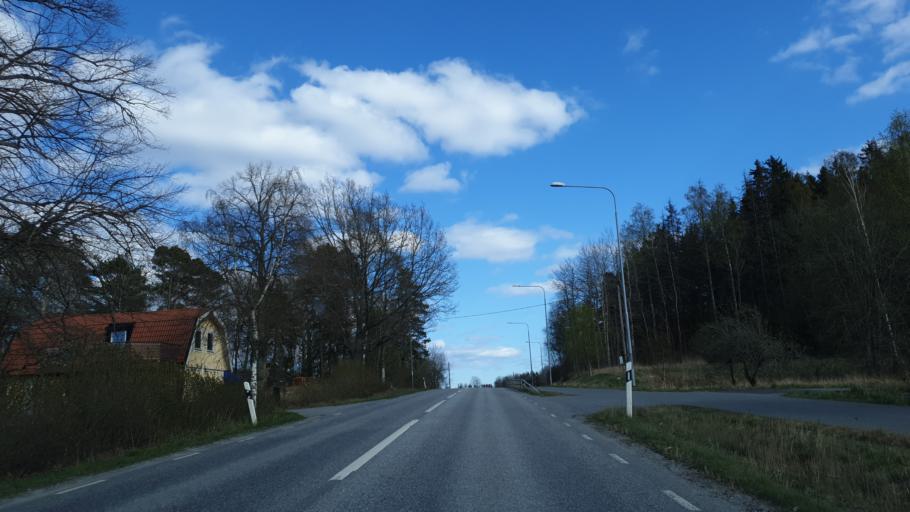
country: SE
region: Stockholm
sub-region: Sigtuna Kommun
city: Marsta
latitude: 59.6086
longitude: 17.8750
